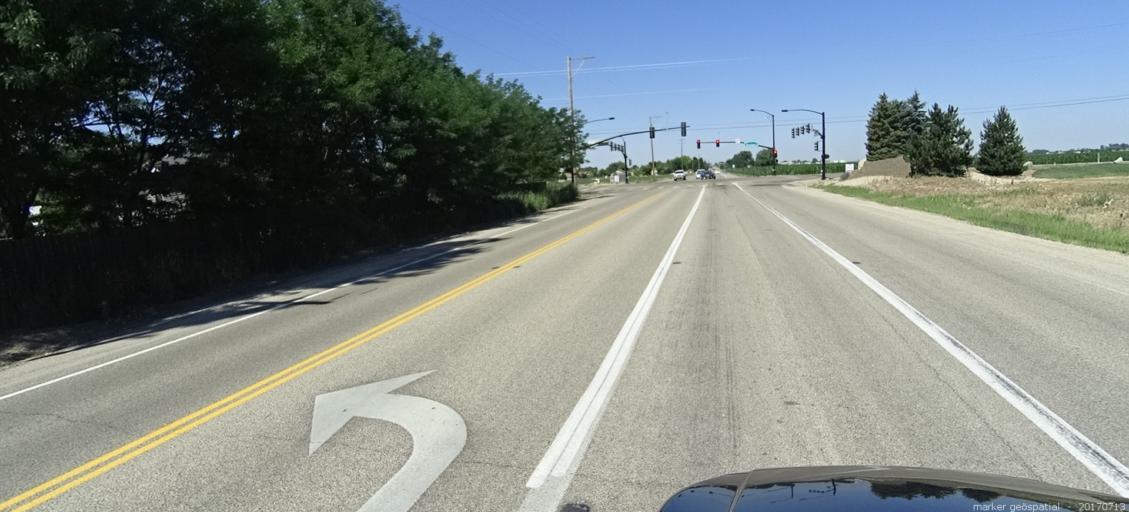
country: US
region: Idaho
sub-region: Ada County
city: Kuna
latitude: 43.5319
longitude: -116.3928
